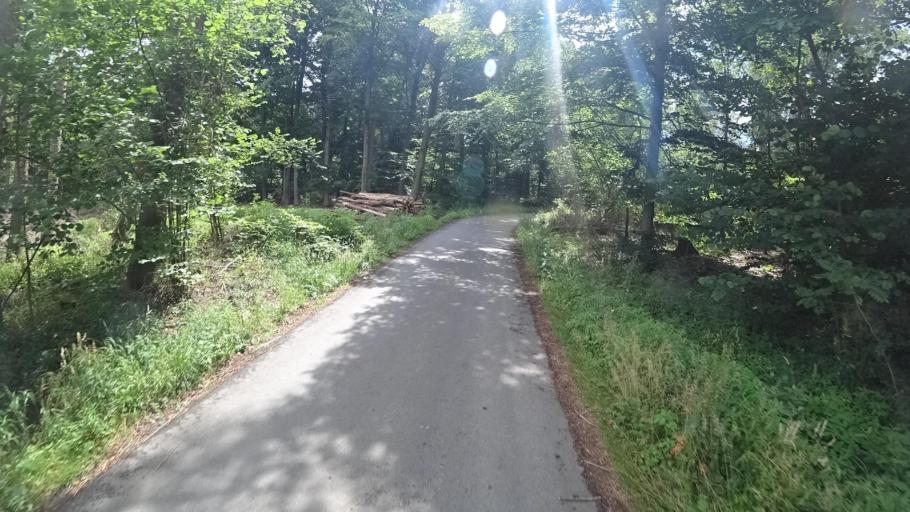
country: DE
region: Rheinland-Pfalz
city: Seifen
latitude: 50.6805
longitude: 7.5096
